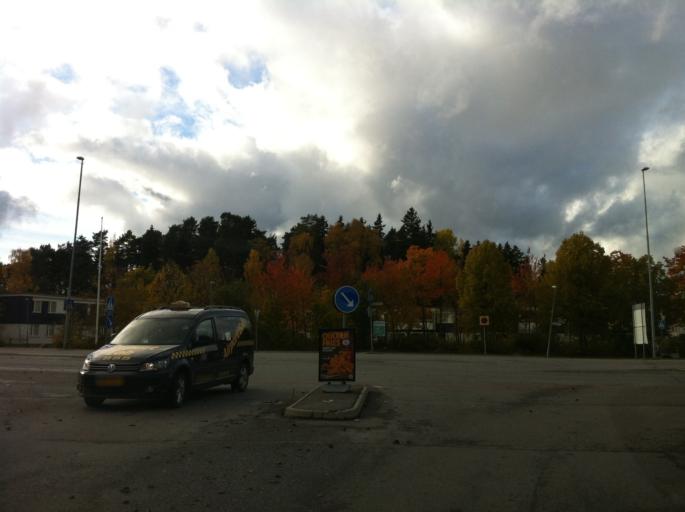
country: SE
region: Stockholm
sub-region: Upplands Vasby Kommun
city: Upplands Vaesby
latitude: 59.5133
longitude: 17.9197
